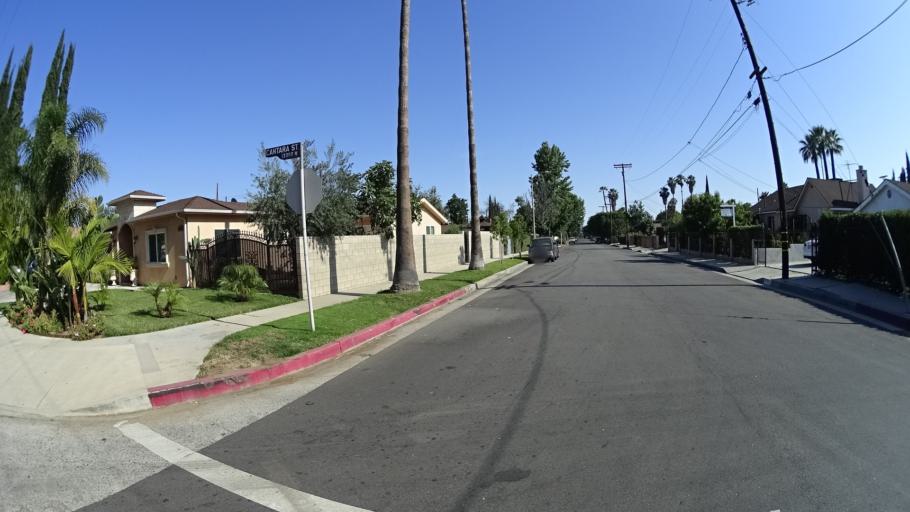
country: US
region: California
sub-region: Los Angeles County
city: Van Nuys
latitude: 34.2197
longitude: -118.4246
